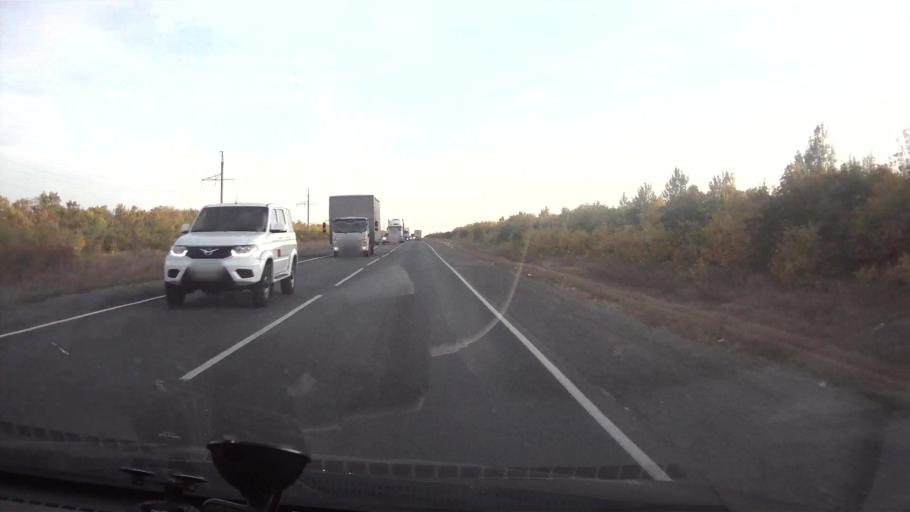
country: RU
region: Saratov
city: Krasnoarmeysk
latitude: 51.1464
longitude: 45.6497
